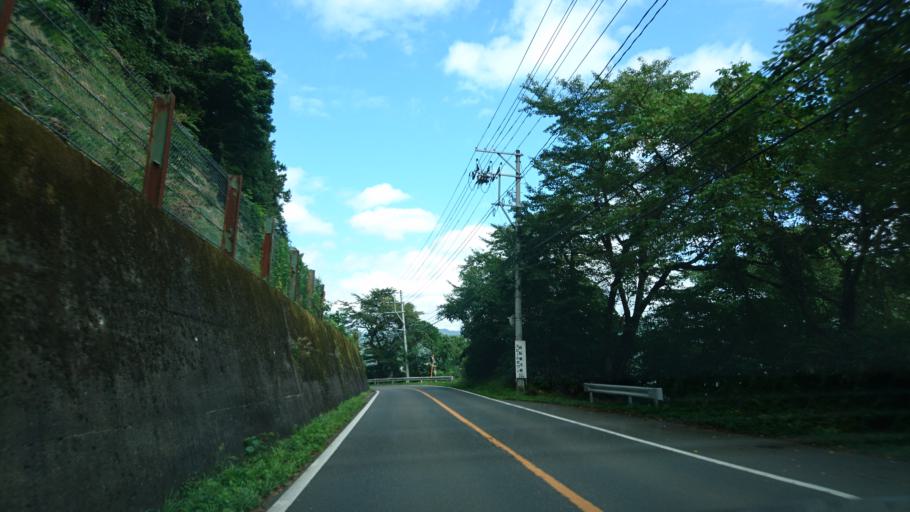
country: JP
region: Miyagi
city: Furukawa
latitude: 38.7831
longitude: 140.8500
